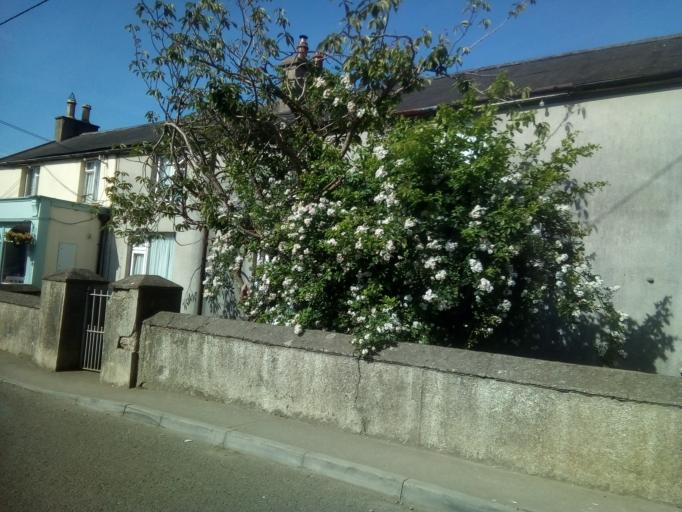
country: IE
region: Leinster
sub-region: Loch Garman
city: Loch Garman
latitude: 52.2317
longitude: -6.5529
